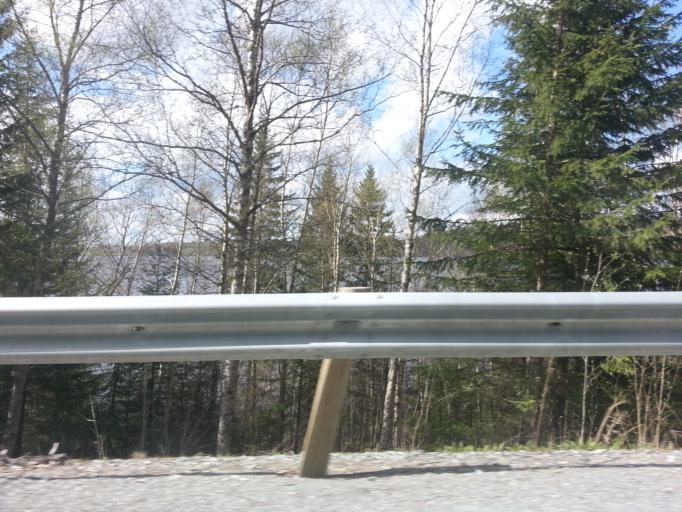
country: NO
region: Nord-Trondelag
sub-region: Levanger
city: Skogn
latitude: 63.6214
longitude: 11.1594
